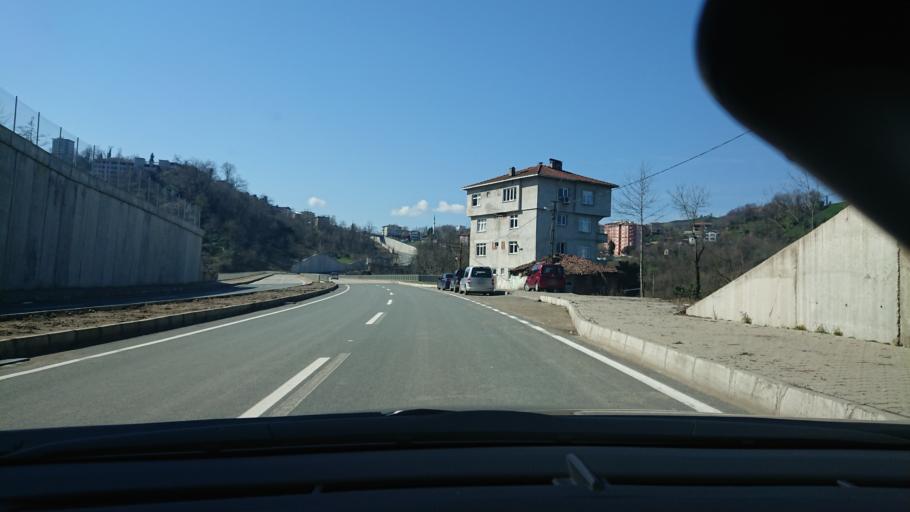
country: TR
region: Rize
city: Rize
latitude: 41.0111
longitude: 40.5063
